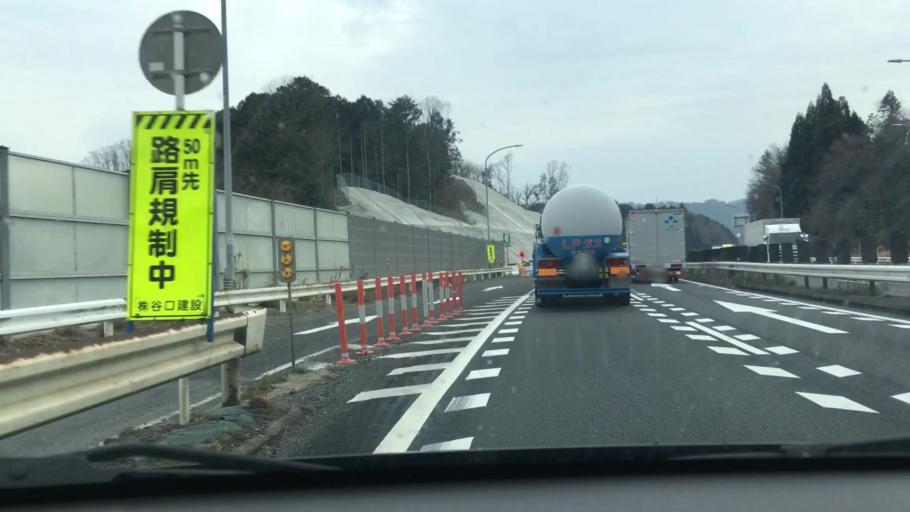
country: JP
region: Mie
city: Kameyama
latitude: 34.8399
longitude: 136.3213
